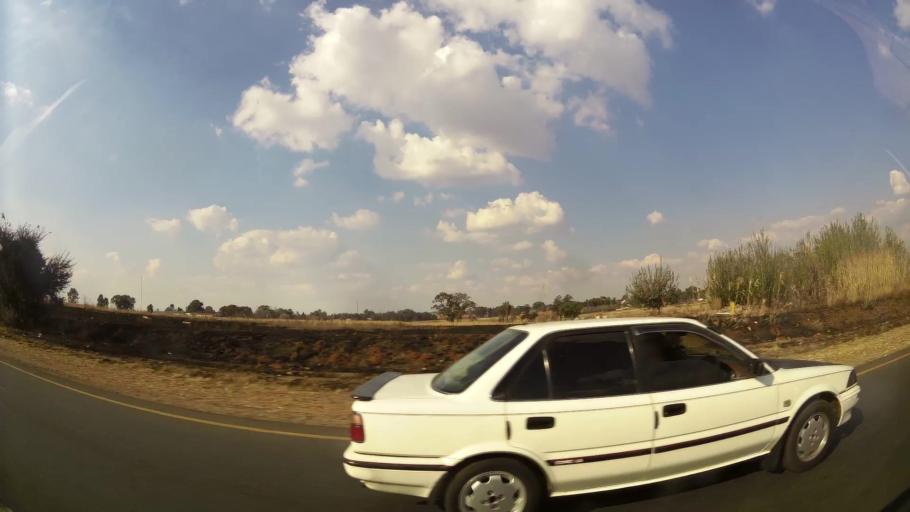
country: ZA
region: Gauteng
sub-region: Ekurhuleni Metropolitan Municipality
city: Brakpan
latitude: -26.2981
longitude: 28.3348
